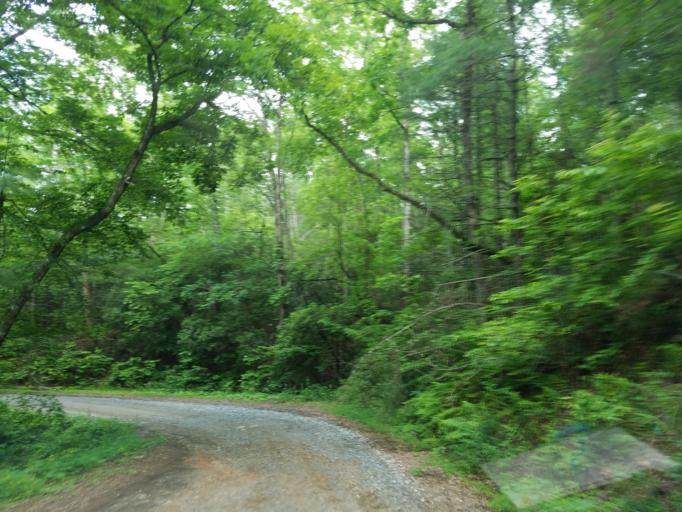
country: US
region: Georgia
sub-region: Dawson County
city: Dawsonville
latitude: 34.5717
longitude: -84.1383
